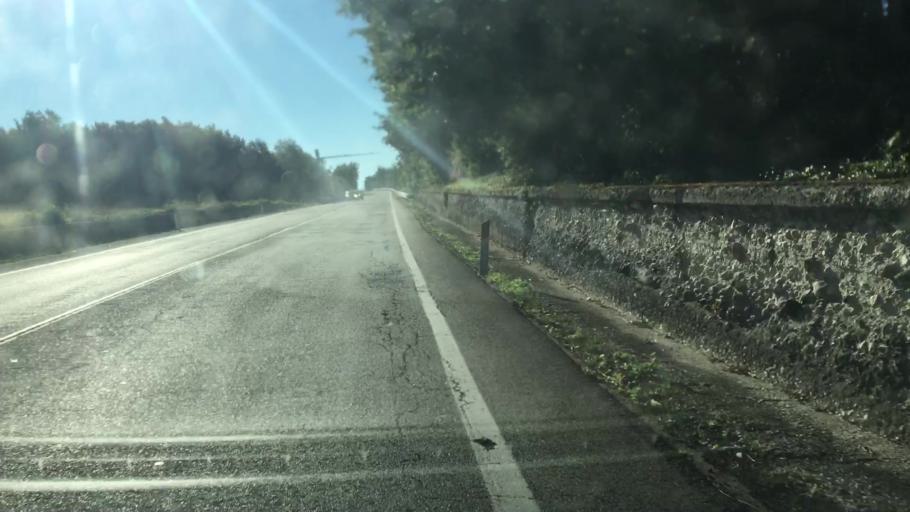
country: IT
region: Molise
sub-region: Provincia di Campobasso
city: Vinchiaturo
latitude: 41.4553
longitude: 14.5810
